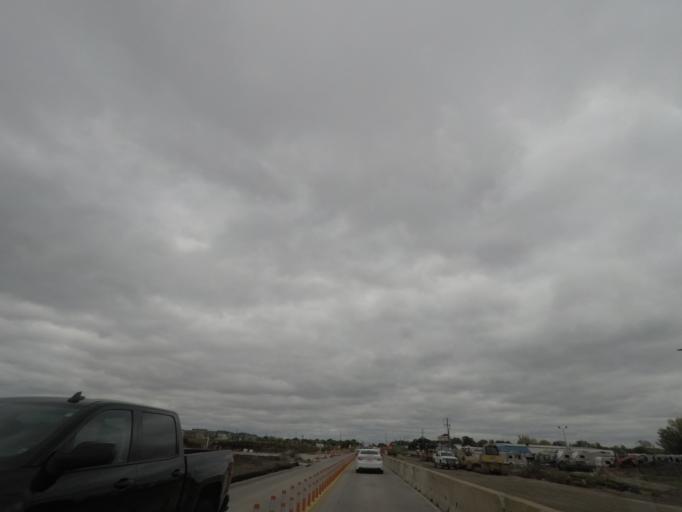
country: US
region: Iowa
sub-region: Polk County
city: Ankeny
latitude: 41.7114
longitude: -93.6006
